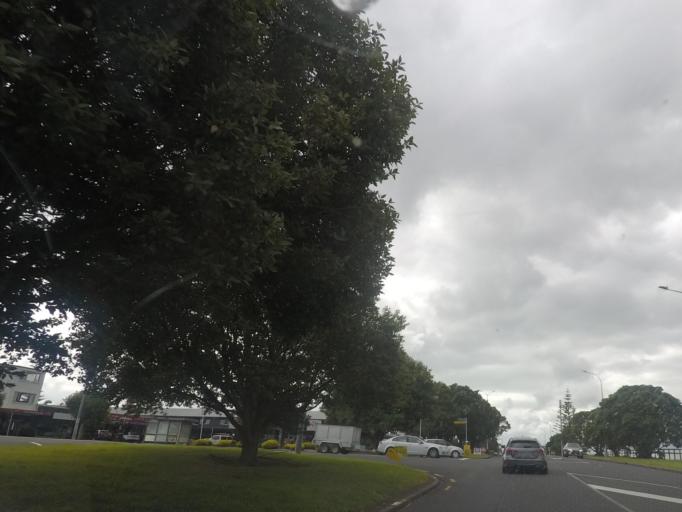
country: NZ
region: Auckland
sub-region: Auckland
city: Tamaki
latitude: -36.8613
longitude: 174.8230
